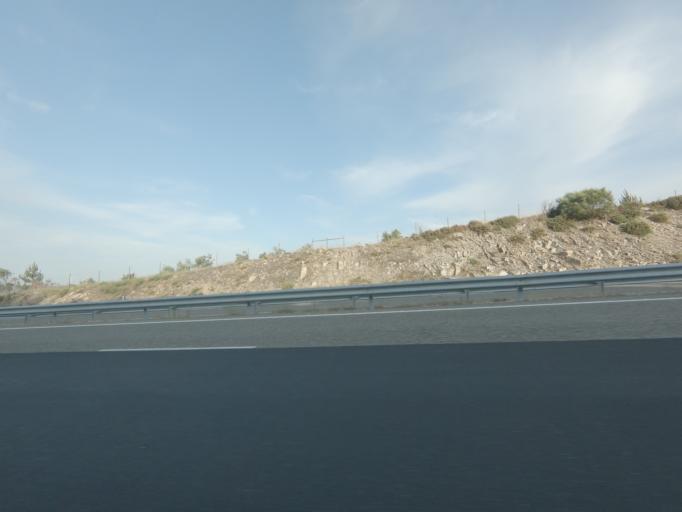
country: PT
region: Vila Real
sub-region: Vila Pouca de Aguiar
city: Vila Pouca de Aguiar
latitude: 41.5205
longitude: -7.6456
